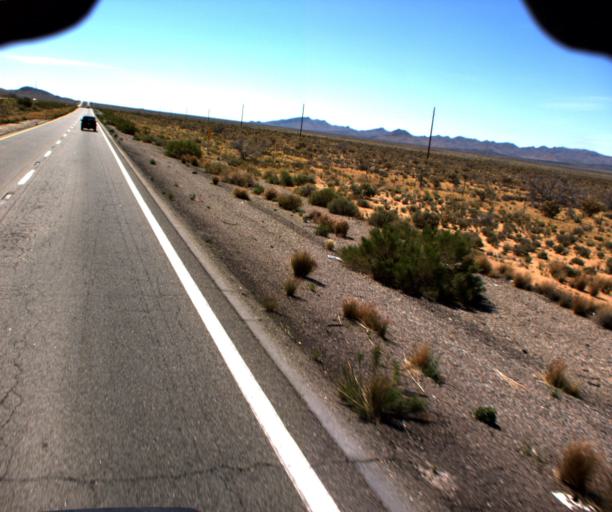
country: US
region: Arizona
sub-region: Mohave County
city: Dolan Springs
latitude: 35.4734
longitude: -114.3138
